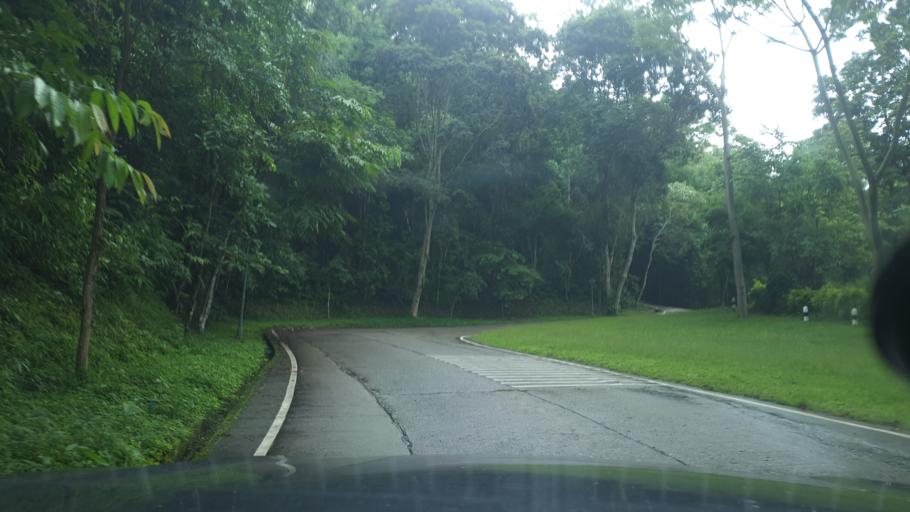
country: TH
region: Chiang Mai
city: Samoeng
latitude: 18.8901
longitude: 98.8624
